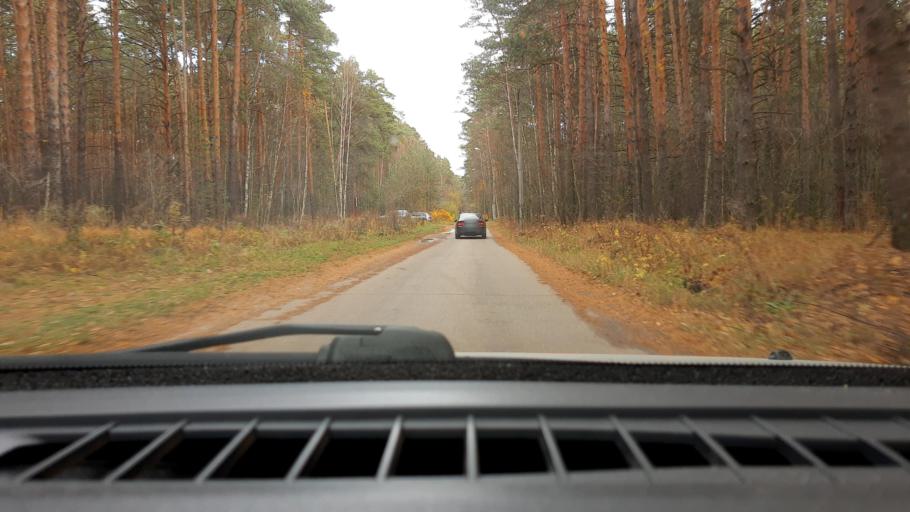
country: RU
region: Nizjnij Novgorod
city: Kstovo
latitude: 56.1680
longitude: 44.1138
